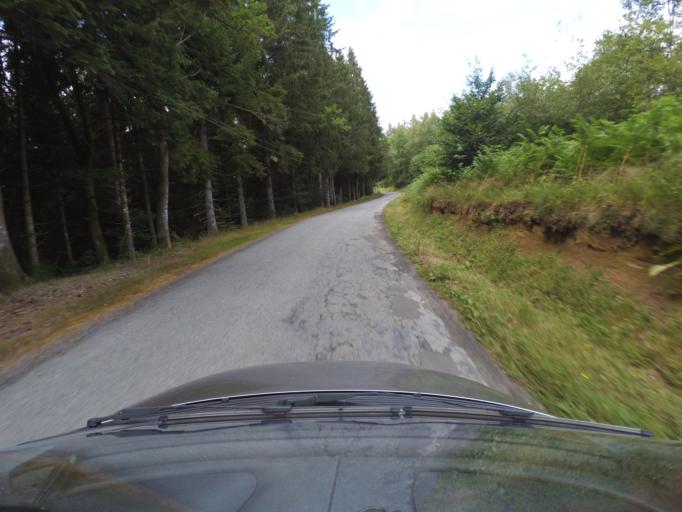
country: FR
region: Limousin
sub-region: Departement de la Creuse
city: Banize
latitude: 45.7649
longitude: 1.9483
